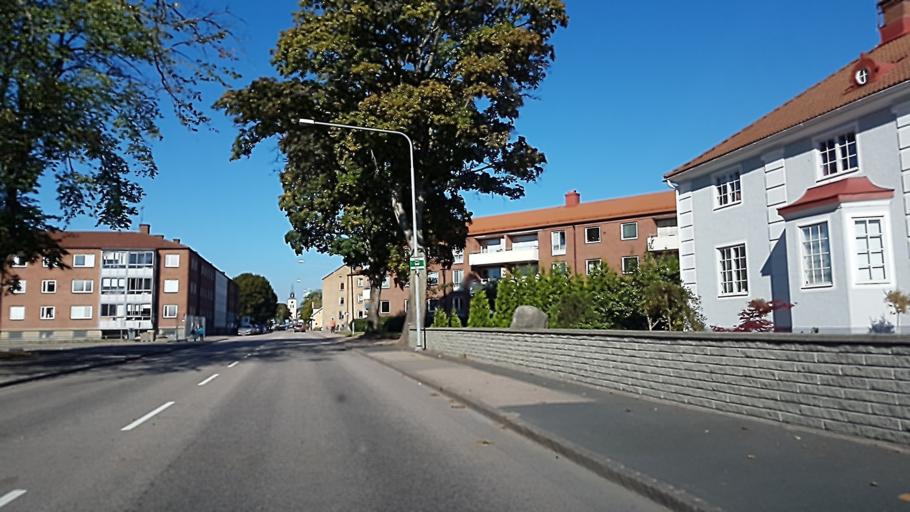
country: SE
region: Kronoberg
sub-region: Ljungby Kommun
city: Ljungby
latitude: 56.8314
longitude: 13.9468
